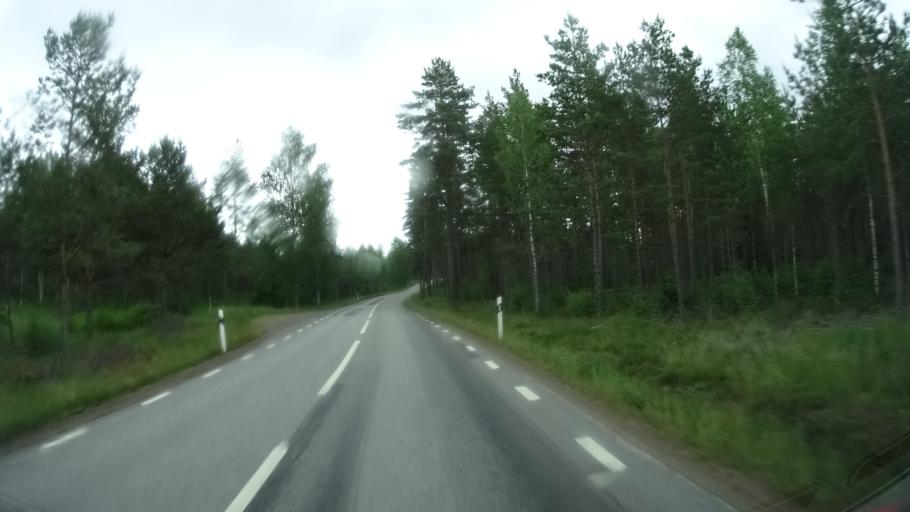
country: SE
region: Kalmar
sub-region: Hultsfreds Kommun
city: Hultsfred
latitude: 57.5314
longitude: 15.7758
